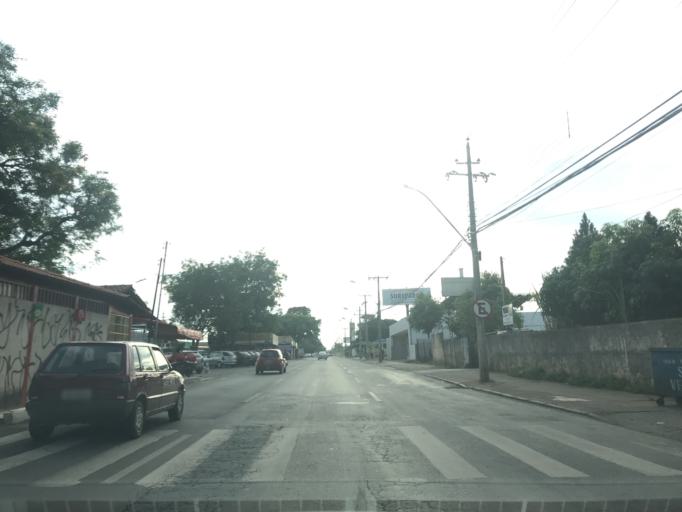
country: BR
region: Federal District
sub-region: Brasilia
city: Brasilia
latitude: -15.8058
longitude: -47.9623
